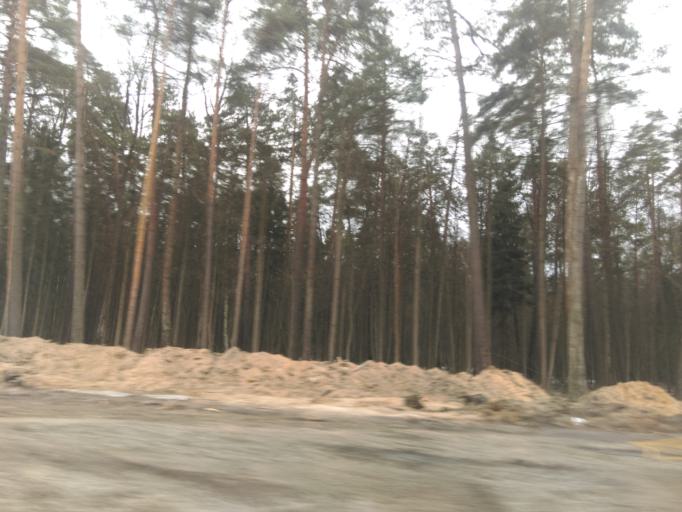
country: RU
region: Moskovskaya
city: Gorki Vtoryye
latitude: 55.7240
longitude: 37.1866
